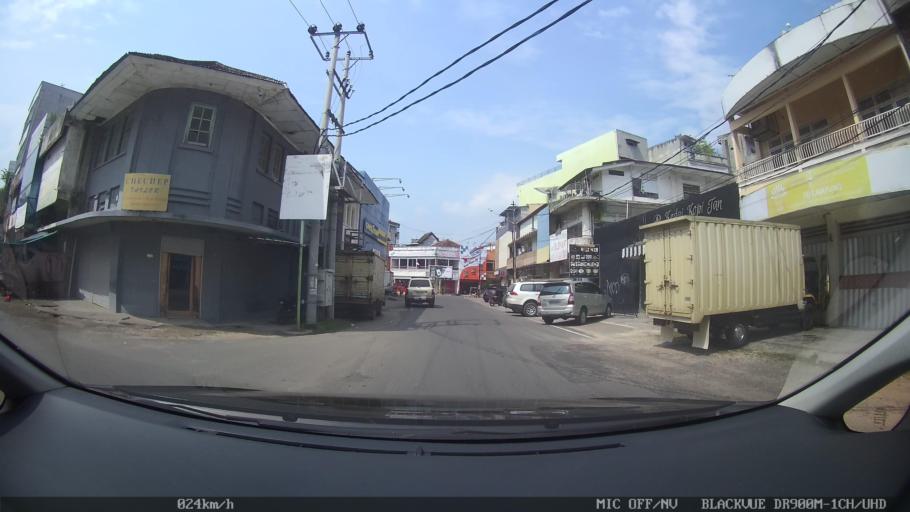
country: ID
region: Lampung
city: Bandarlampung
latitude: -5.4483
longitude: 105.2641
